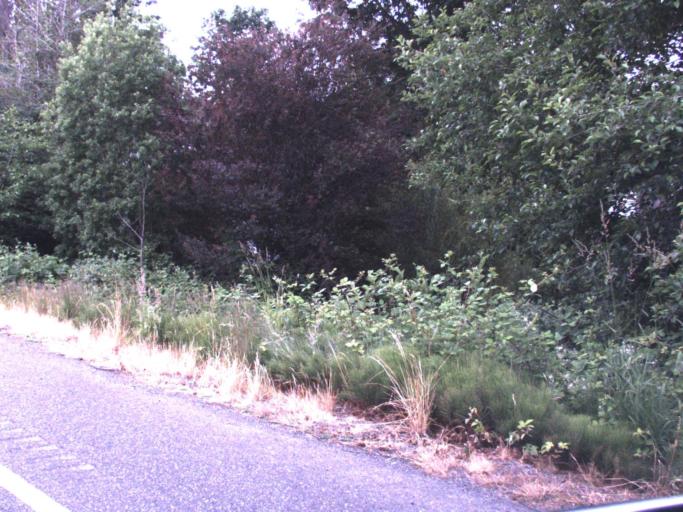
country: US
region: Washington
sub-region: Whatcom County
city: Birch Bay
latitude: 48.8920
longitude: -122.6779
